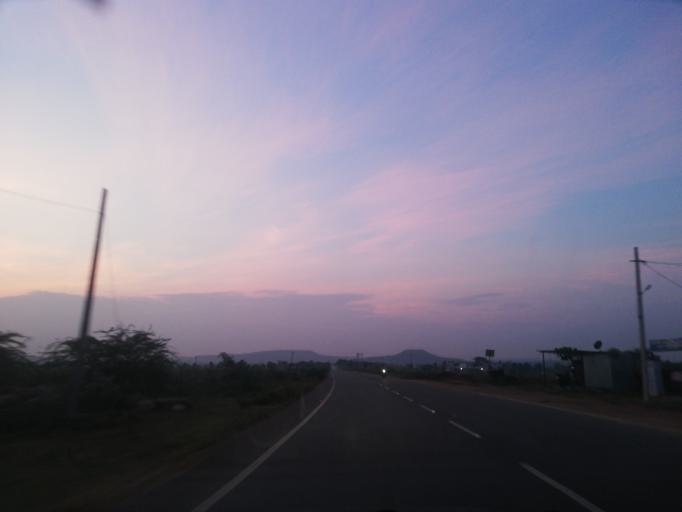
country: IN
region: Andhra Pradesh
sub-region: Guntur
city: Macherla
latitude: 16.6878
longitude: 79.2521
